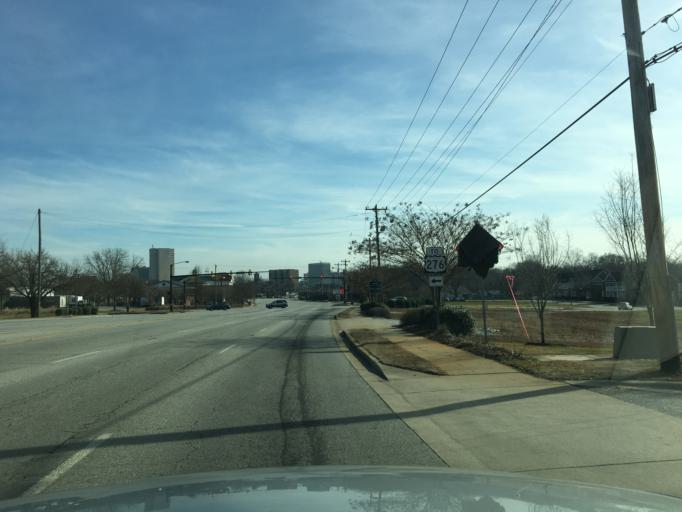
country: US
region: South Carolina
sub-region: Greenville County
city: Greenville
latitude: 34.8621
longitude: -82.4078
